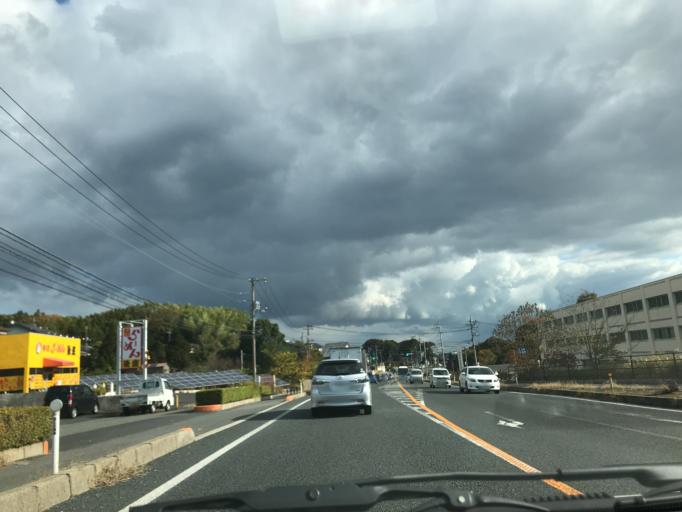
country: JP
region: Shimane
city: Yasugicho
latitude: 35.4329
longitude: 133.1626
